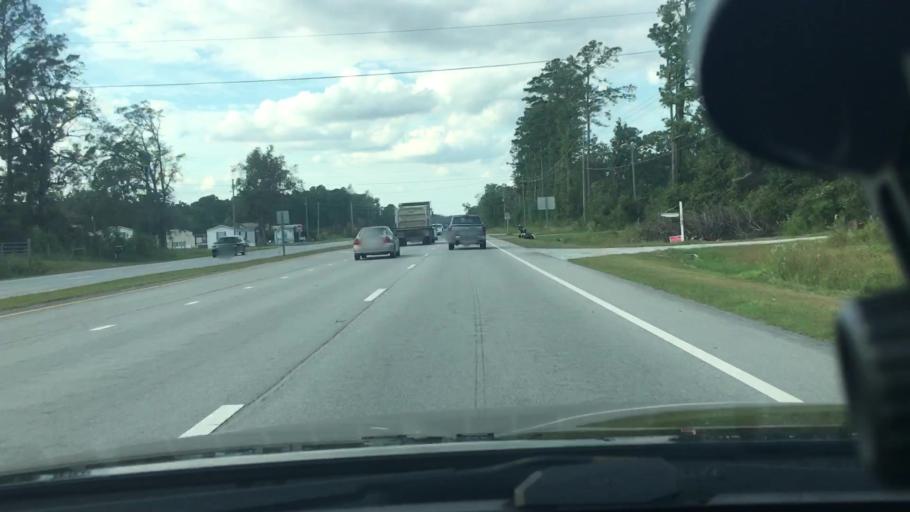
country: US
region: North Carolina
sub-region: Craven County
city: New Bern
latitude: 35.1453
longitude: -77.0314
